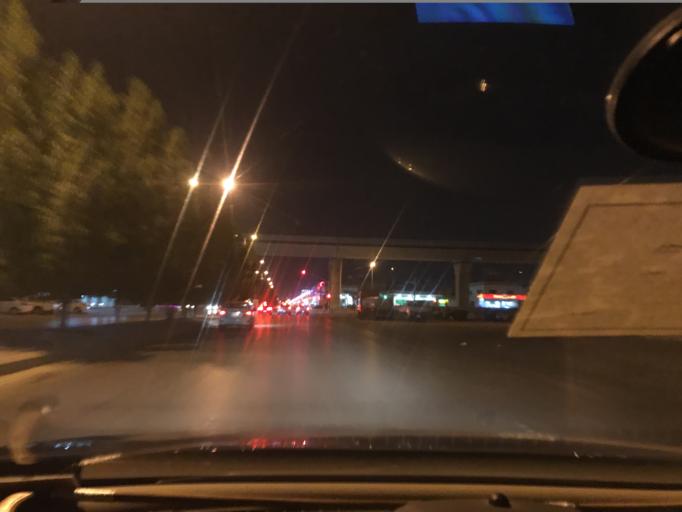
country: SA
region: Ar Riyad
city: Riyadh
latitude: 24.7469
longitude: 46.7959
